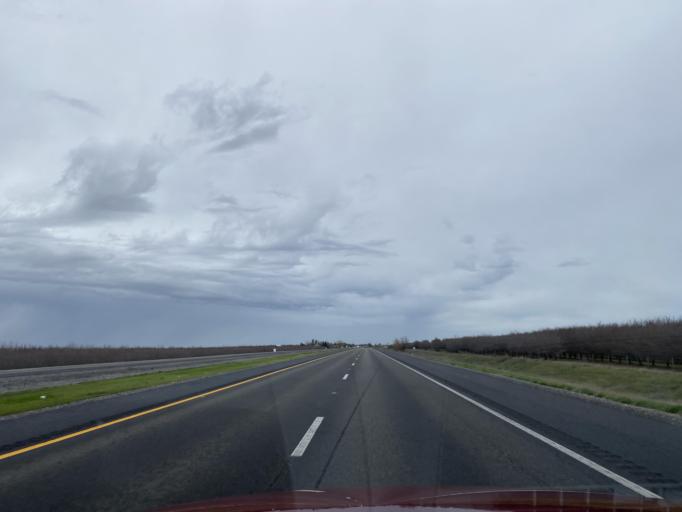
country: US
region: California
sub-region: Tehama County
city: Corning
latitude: 39.9895
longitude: -122.2043
